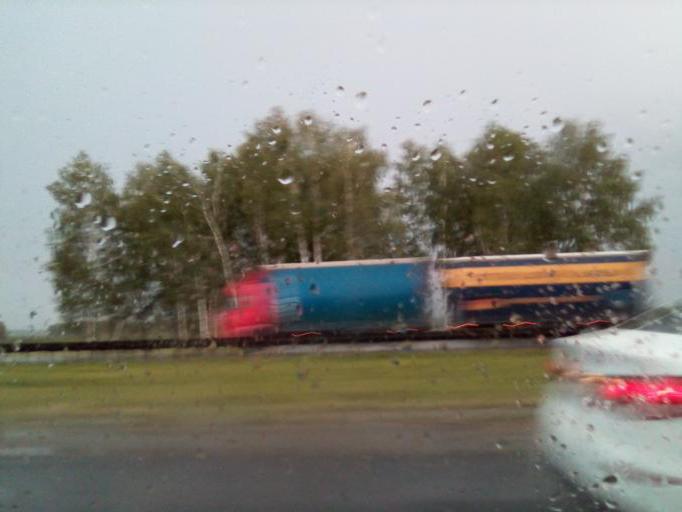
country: RU
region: Chelyabinsk
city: Poletayevo
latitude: 54.9763
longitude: 60.9889
